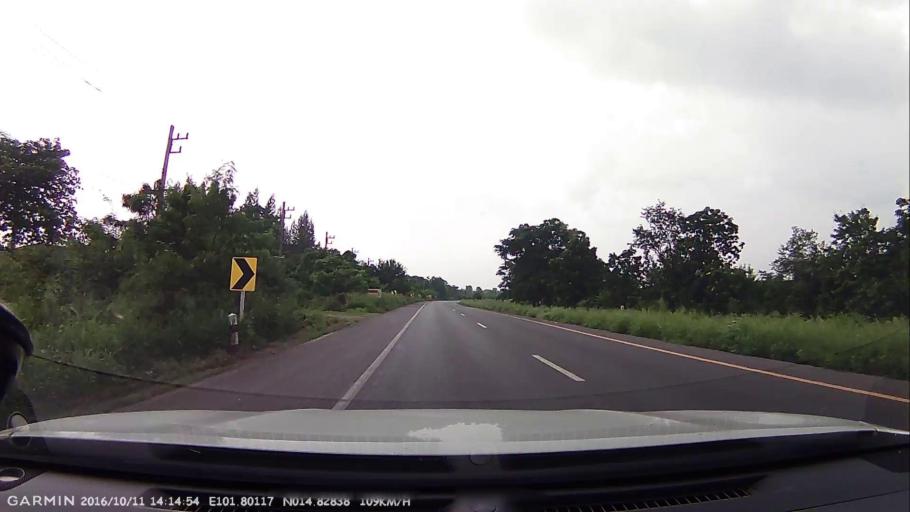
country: TH
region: Nakhon Ratchasima
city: Sung Noen
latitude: 14.8284
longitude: 101.8012
